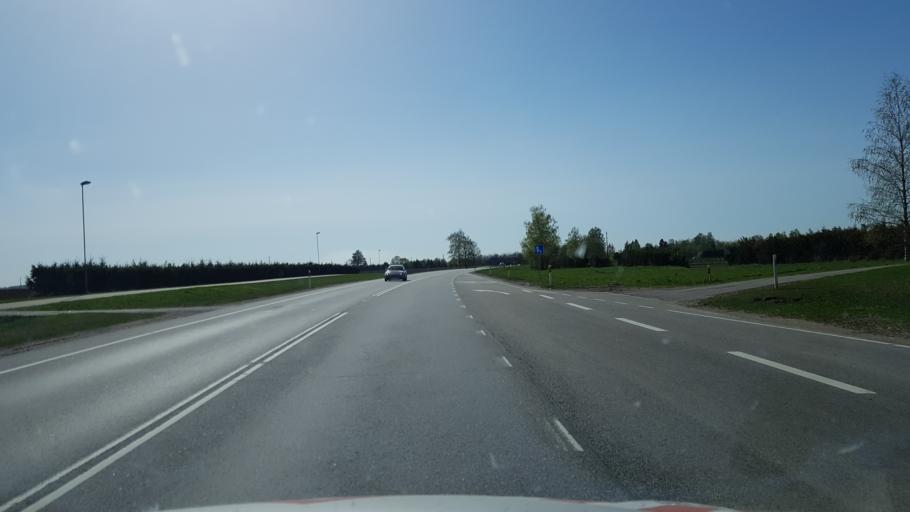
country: EE
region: Viljandimaa
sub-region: Viljandi linn
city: Viljandi
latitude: 58.3478
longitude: 25.5216
